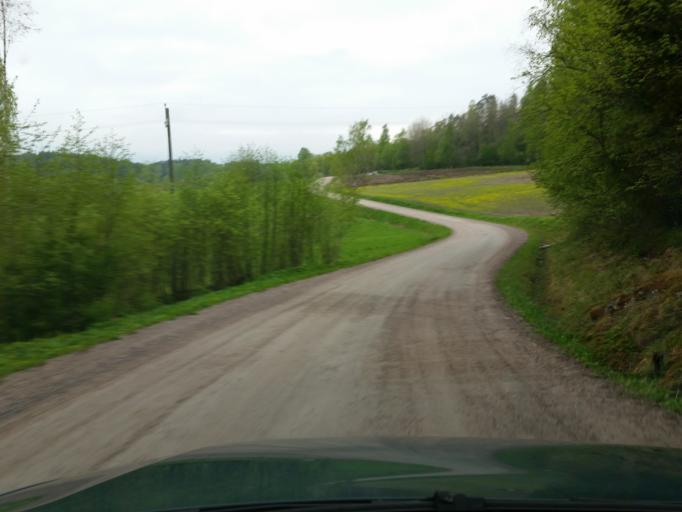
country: FI
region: Uusimaa
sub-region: Helsinki
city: Karjalohja
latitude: 60.1836
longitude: 23.6835
